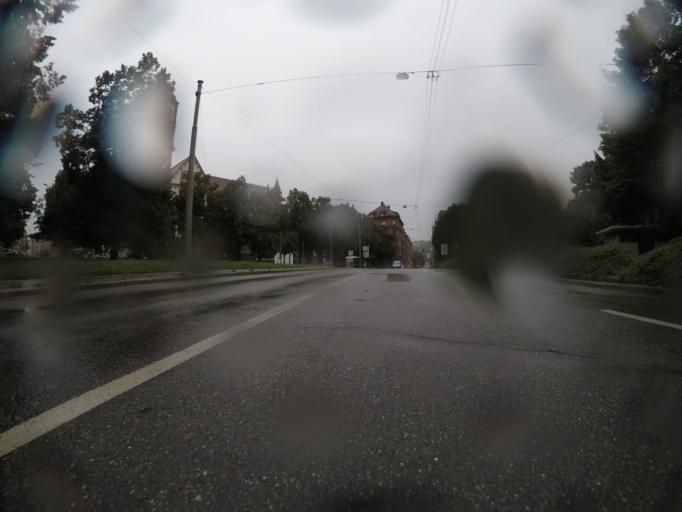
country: DE
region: Baden-Wuerttemberg
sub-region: Regierungsbezirk Stuttgart
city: Stuttgart
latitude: 48.7732
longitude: 9.1563
